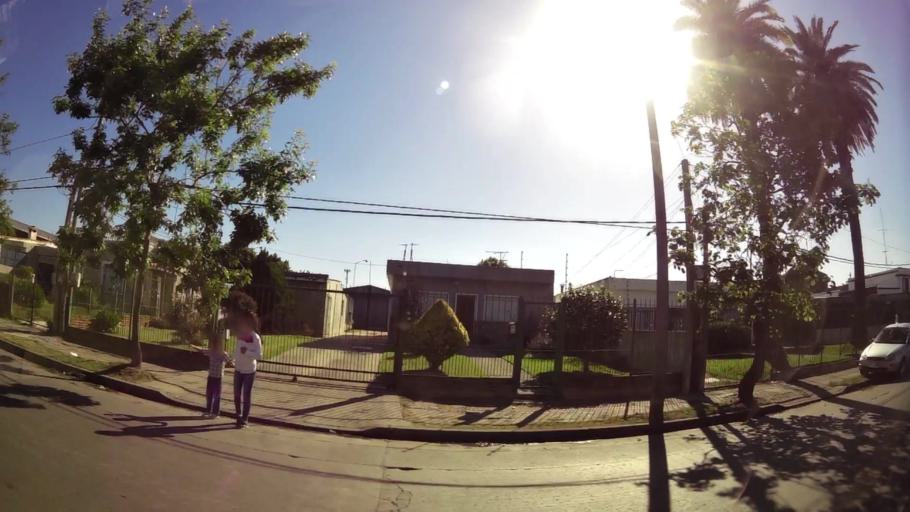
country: UY
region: Montevideo
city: Montevideo
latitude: -34.8355
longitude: -56.1506
